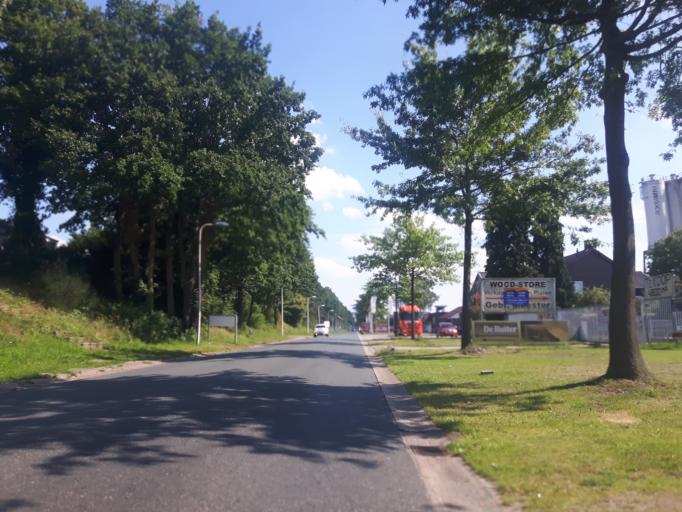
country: NL
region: Overijssel
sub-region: Gemeente Enschede
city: Enschede
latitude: 52.2311
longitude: 6.8457
